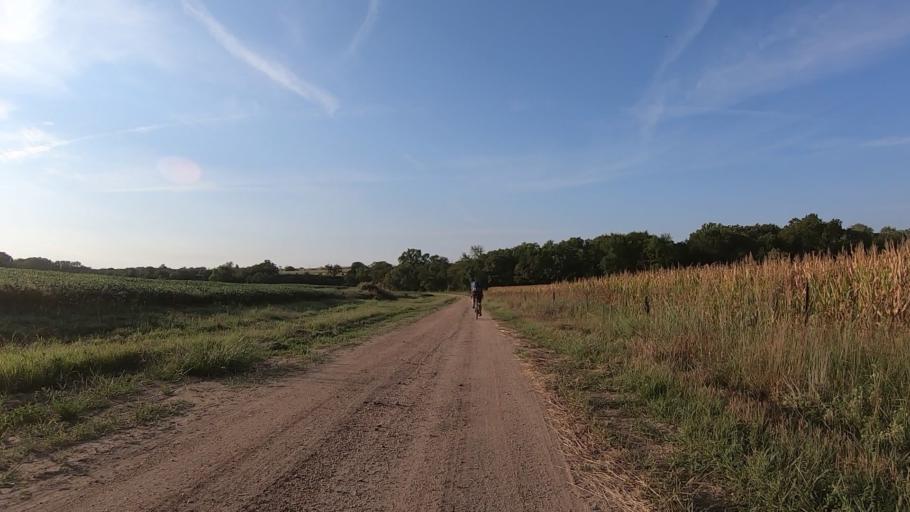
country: US
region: Kansas
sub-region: Marshall County
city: Blue Rapids
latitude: 39.7233
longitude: -96.8070
